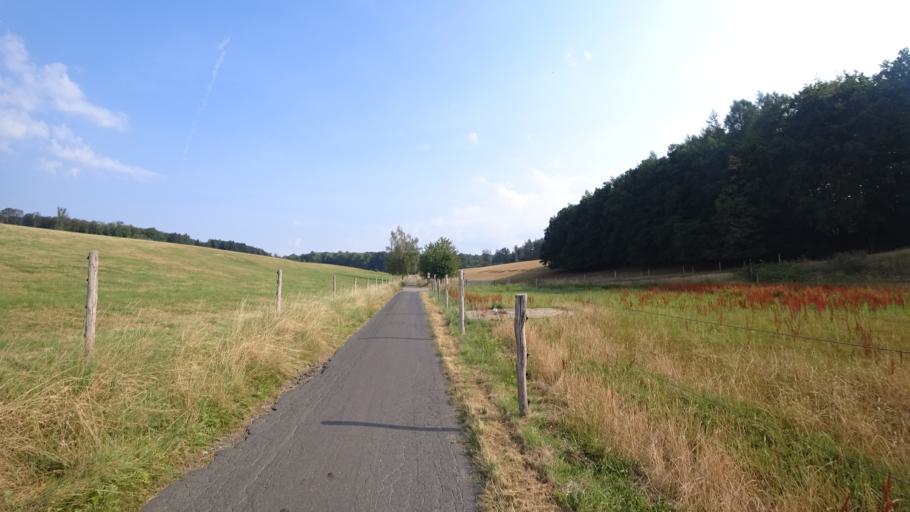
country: DE
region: Rheinland-Pfalz
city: Hundsdorf
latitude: 50.4736
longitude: 7.7052
